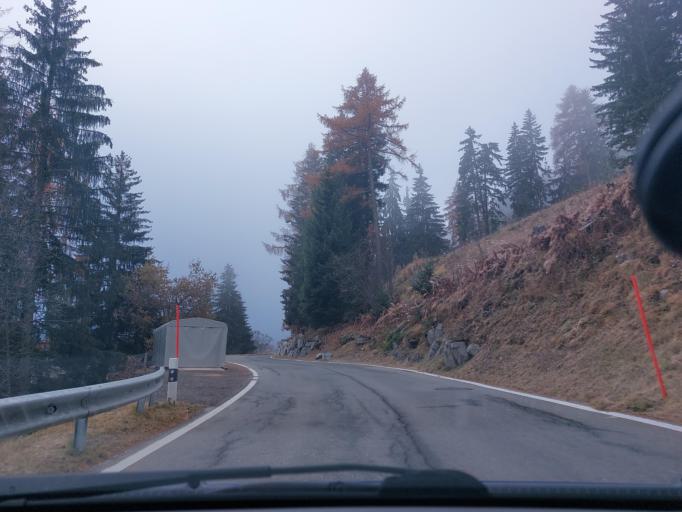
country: CH
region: Valais
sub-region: Conthey District
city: Basse-Nendaz
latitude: 46.1587
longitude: 7.3133
